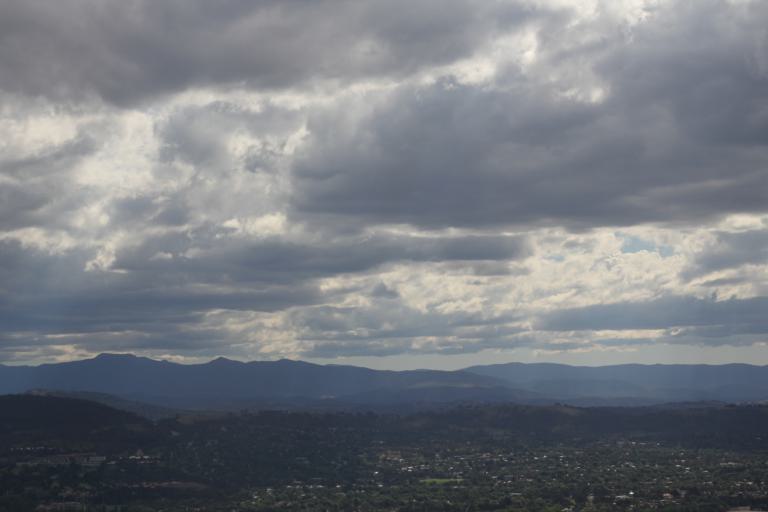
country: AU
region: Australian Capital Territory
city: Canberra
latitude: -35.2775
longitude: 149.1950
